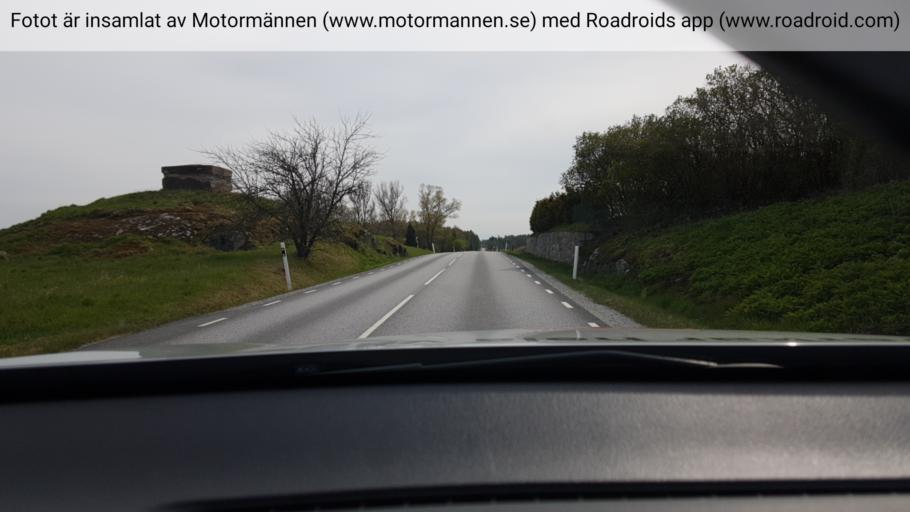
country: SE
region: Stockholm
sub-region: Sigtuna Kommun
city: Rosersberg
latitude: 59.6057
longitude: 17.9854
